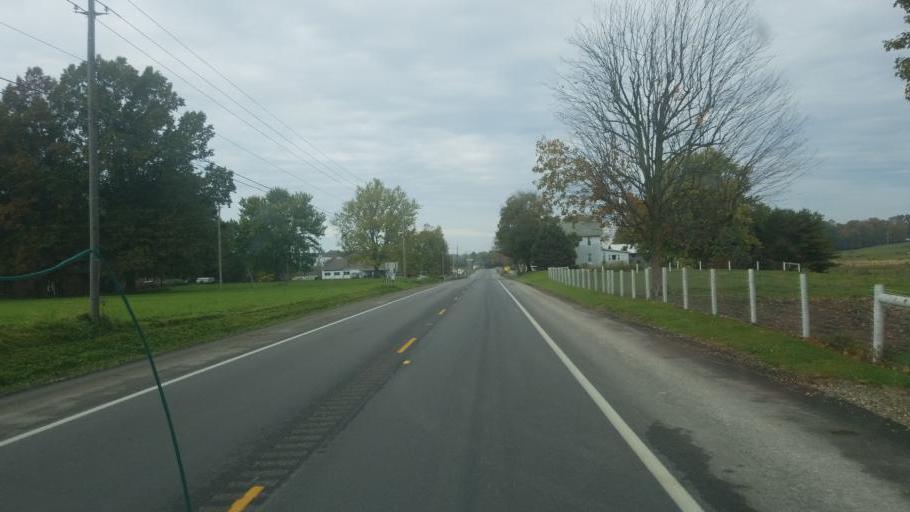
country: US
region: Ohio
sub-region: Wayne County
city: Apple Creek
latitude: 40.7177
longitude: -81.7642
